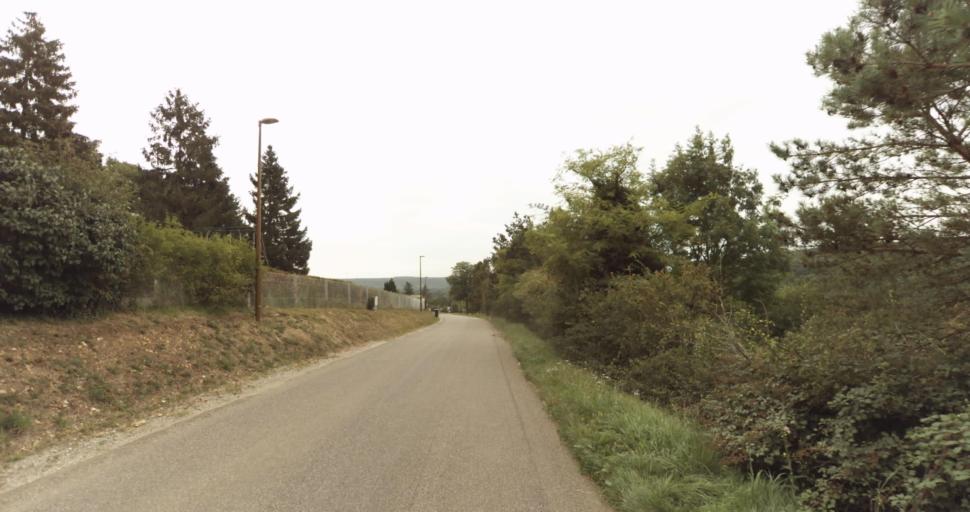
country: FR
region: Haute-Normandie
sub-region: Departement de l'Eure
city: Marcilly-sur-Eure
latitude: 48.8286
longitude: 1.3319
